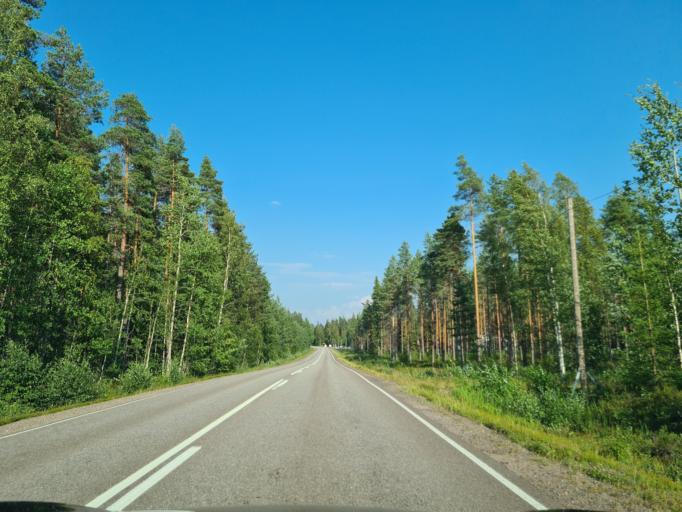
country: FI
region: Satakunta
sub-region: Pohjois-Satakunta
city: Karvia
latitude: 62.3259
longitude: 22.6916
